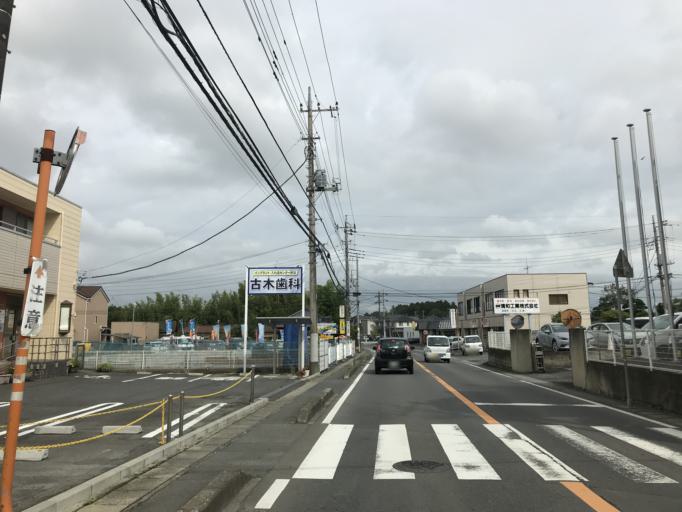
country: JP
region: Ibaraki
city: Mito-shi
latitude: 36.3250
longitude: 140.4513
